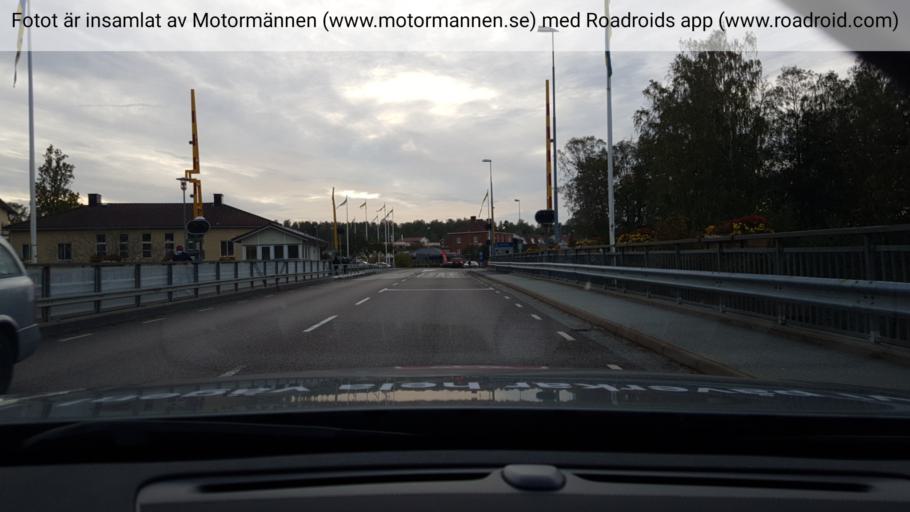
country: SE
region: Vaestra Goetaland
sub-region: Bengtsfors Kommun
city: Bengtsfors
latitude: 59.0293
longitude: 12.2303
